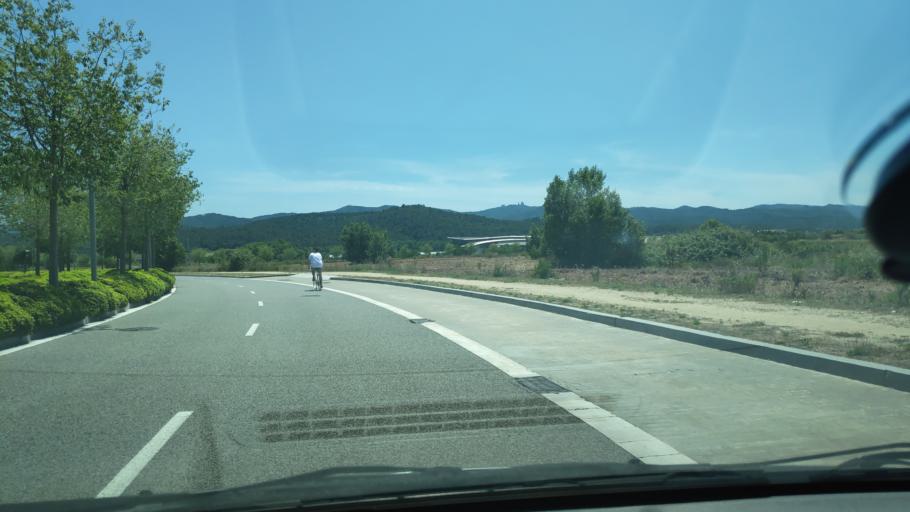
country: ES
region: Catalonia
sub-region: Provincia de Barcelona
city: Barbera del Valles
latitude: 41.4901
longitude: 2.1100
